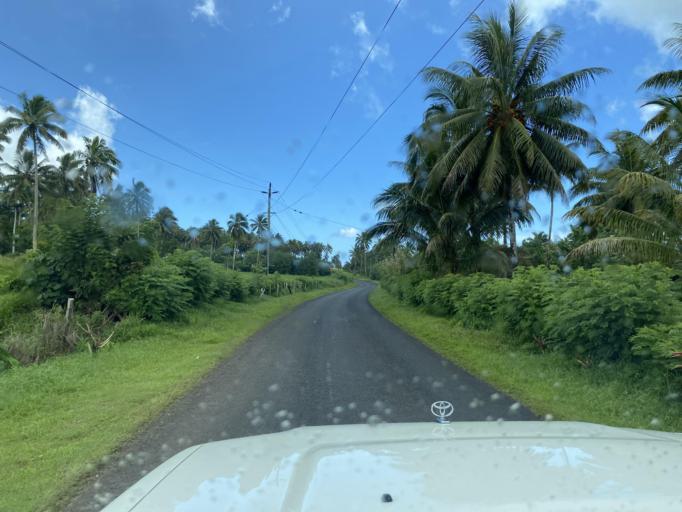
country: WS
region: Va`a-o-Fonoti
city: Samamea
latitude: -13.9809
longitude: -171.5879
